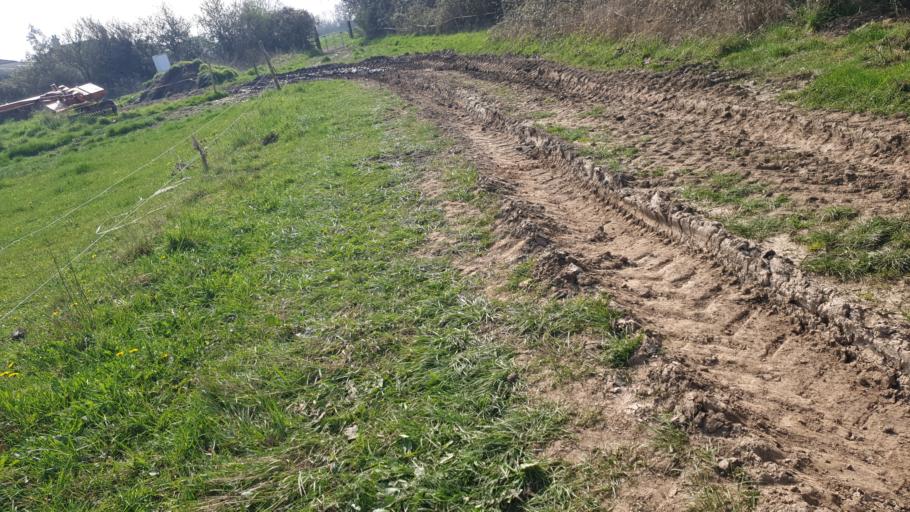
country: GB
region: England
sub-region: Essex
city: Mistley
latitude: 51.9237
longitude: 1.1585
